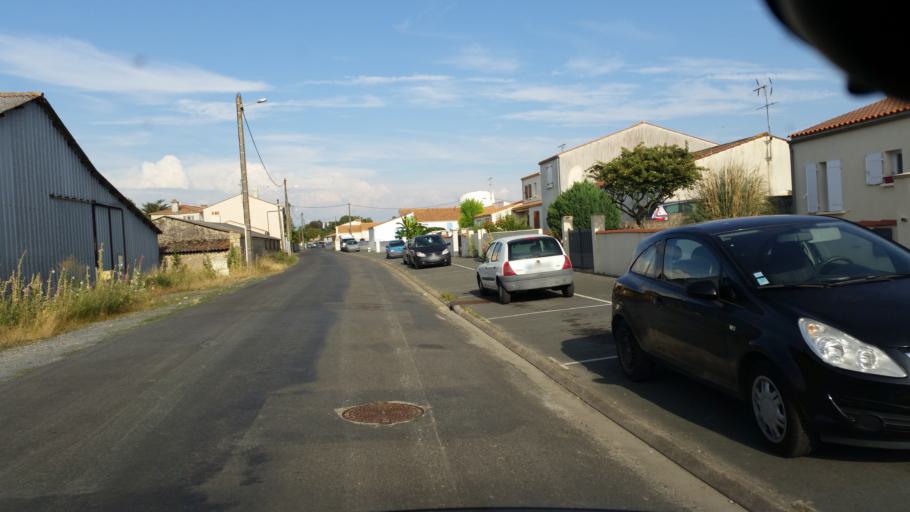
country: FR
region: Poitou-Charentes
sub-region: Departement de la Charente-Maritime
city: Marans
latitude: 46.3098
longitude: -1.0031
